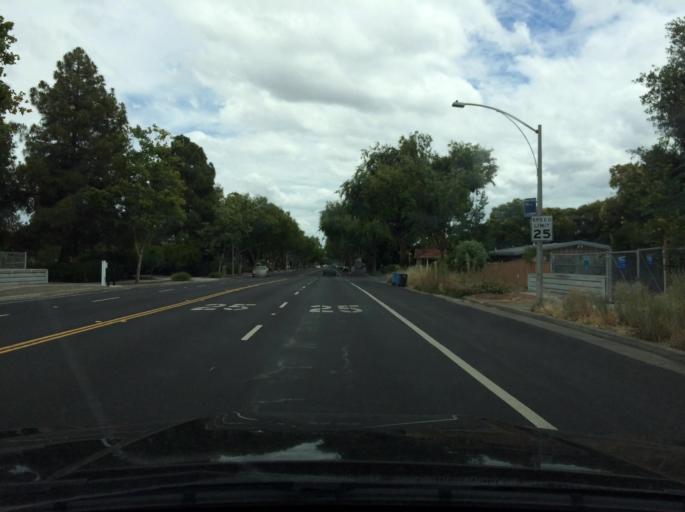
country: US
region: California
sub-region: Santa Clara County
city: Palo Alto
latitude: 37.4267
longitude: -122.1186
